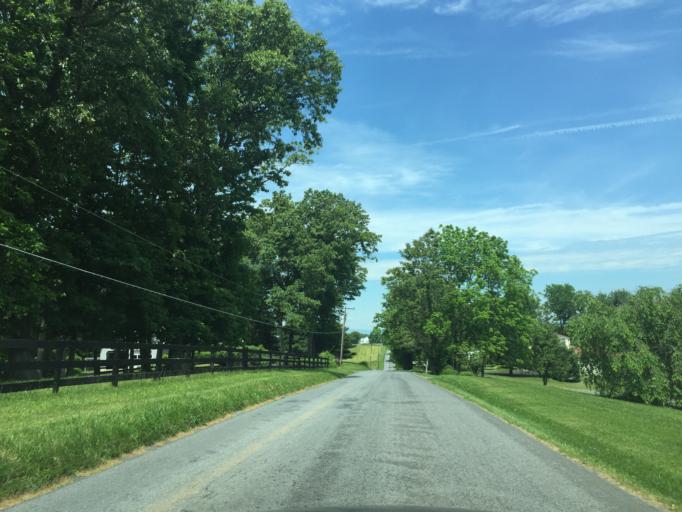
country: US
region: Virginia
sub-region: Warren County
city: Shenandoah Farms
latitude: 38.9824
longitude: -78.1322
